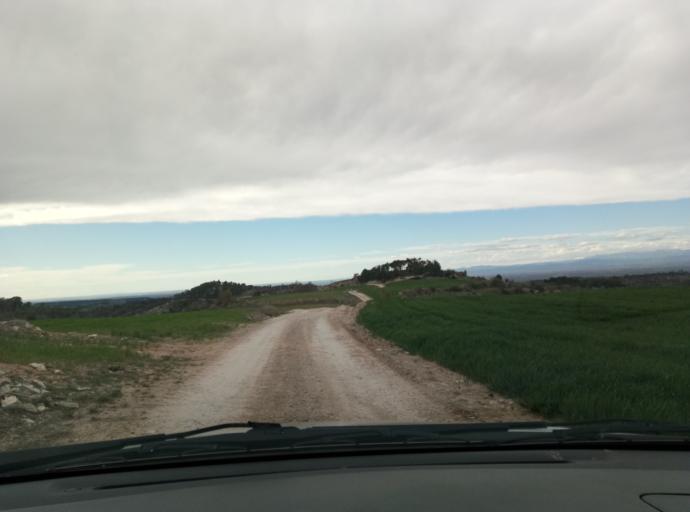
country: ES
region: Catalonia
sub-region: Provincia de Lleida
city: Nalec
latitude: 41.5165
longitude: 1.1411
